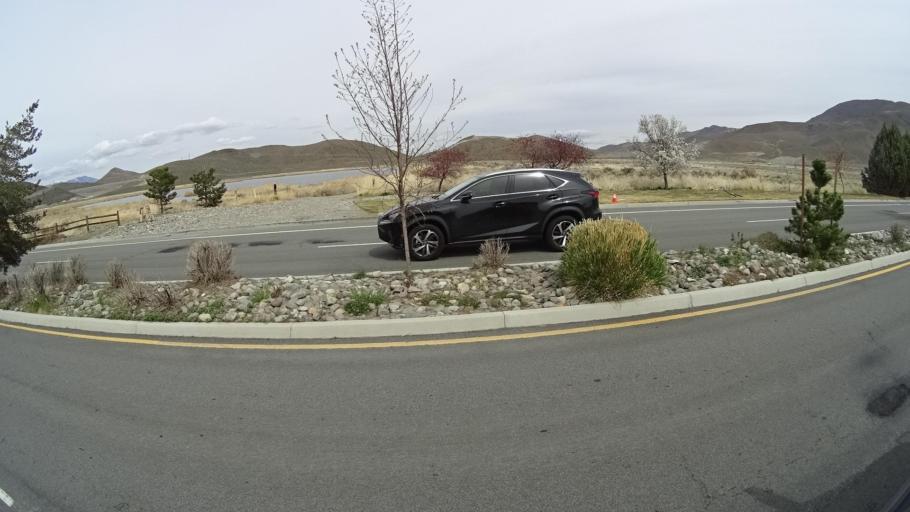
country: US
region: Nevada
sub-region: Washoe County
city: Sparks
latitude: 39.4525
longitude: -119.7340
